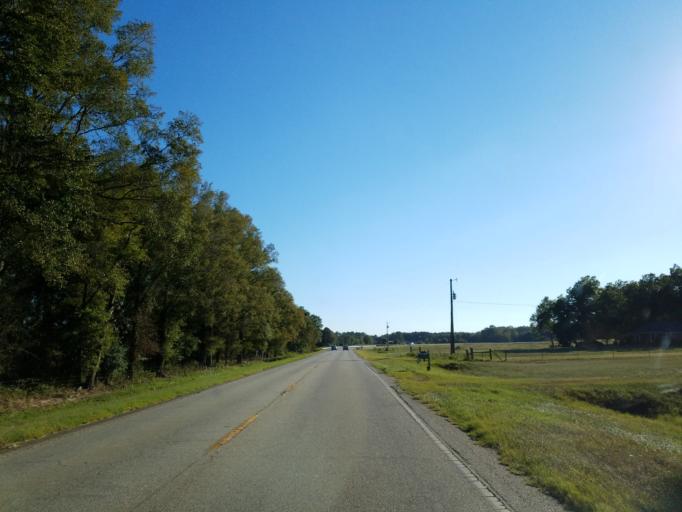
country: US
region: Georgia
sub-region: Lee County
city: Leesburg
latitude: 31.7535
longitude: -84.1550
